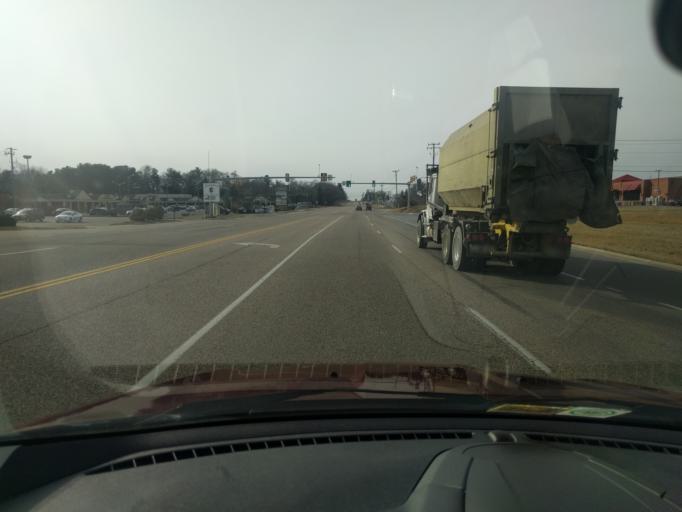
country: US
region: Virginia
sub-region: Augusta County
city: Stuarts Draft
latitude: 38.0382
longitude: -79.0246
